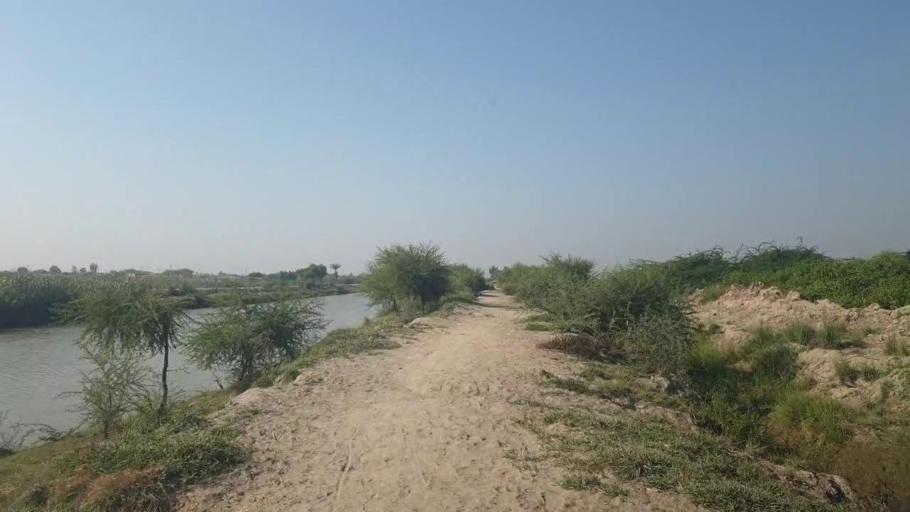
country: PK
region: Sindh
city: Badin
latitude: 24.6976
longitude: 68.8758
